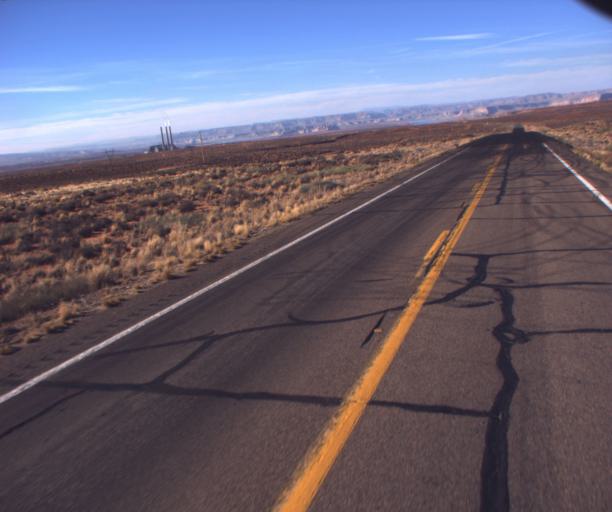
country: US
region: Arizona
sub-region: Coconino County
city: LeChee
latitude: 36.8675
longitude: -111.3406
